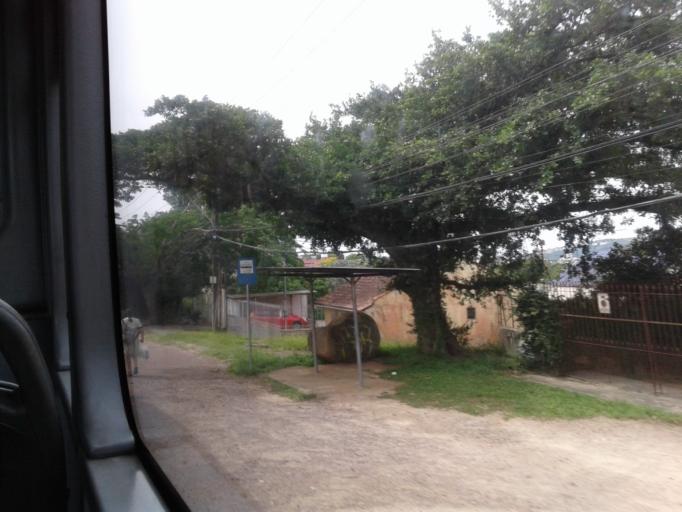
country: BR
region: Rio Grande do Sul
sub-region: Porto Alegre
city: Porto Alegre
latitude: -30.1239
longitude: -51.2239
